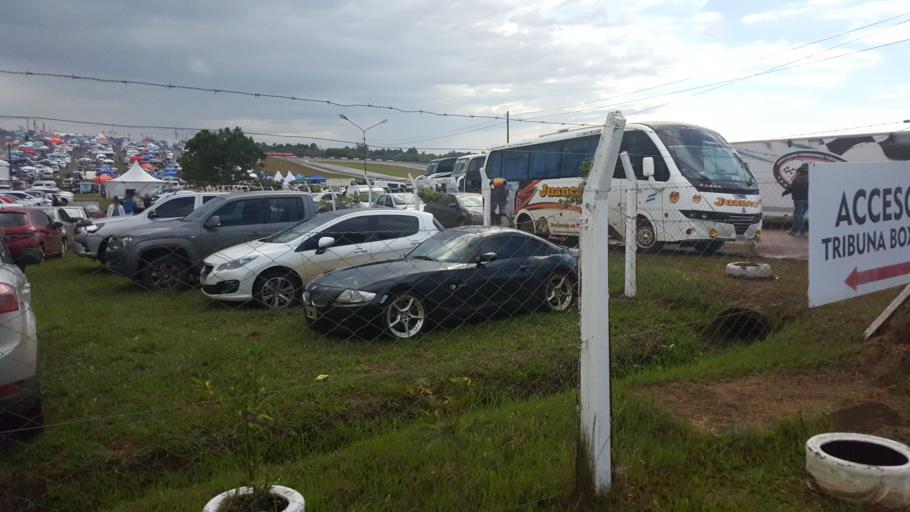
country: AR
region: Misiones
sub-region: Departamento de Capital
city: Posadas
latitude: -27.4382
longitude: -55.9260
